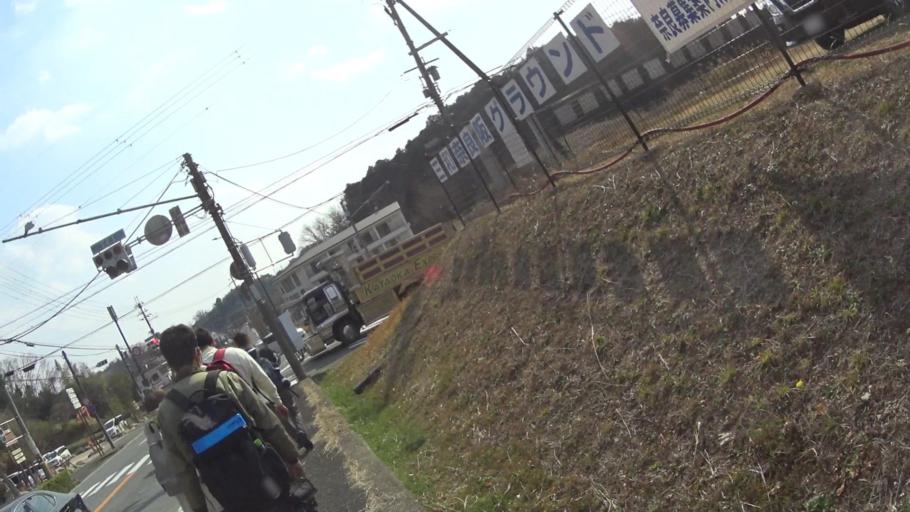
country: JP
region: Nara
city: Nara-shi
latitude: 34.7071
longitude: 135.8275
